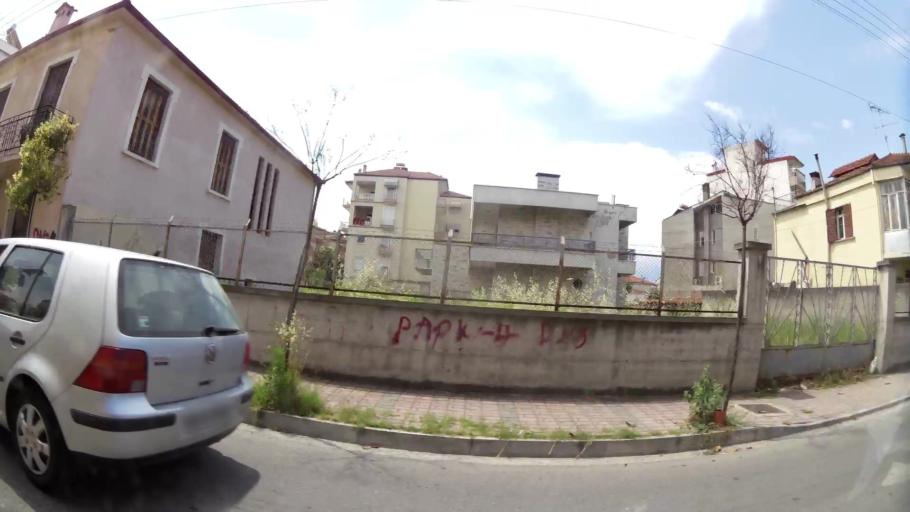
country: GR
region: Central Macedonia
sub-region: Nomos Pierias
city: Katerini
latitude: 40.2683
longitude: 22.5026
